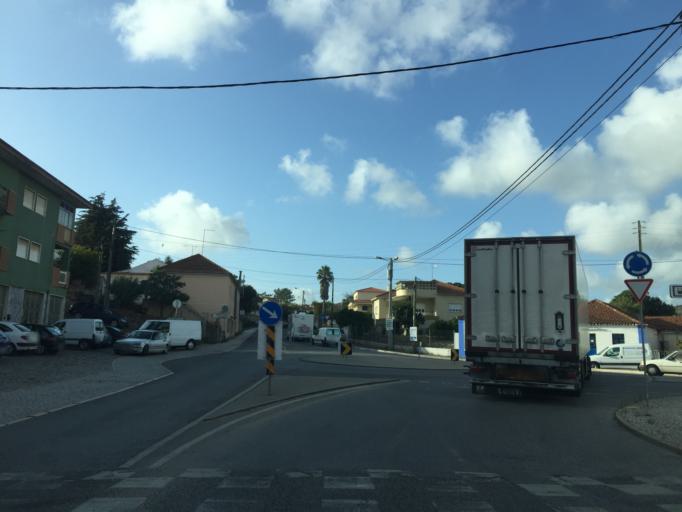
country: PT
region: Lisbon
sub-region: Torres Vedras
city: Torres Vedras
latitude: 39.1020
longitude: -9.2590
